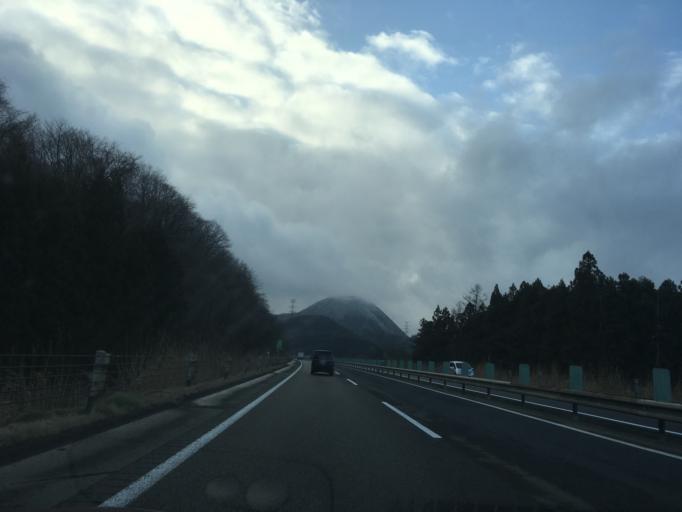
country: JP
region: Miyagi
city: Shiroishi
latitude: 38.1813
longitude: 140.6073
